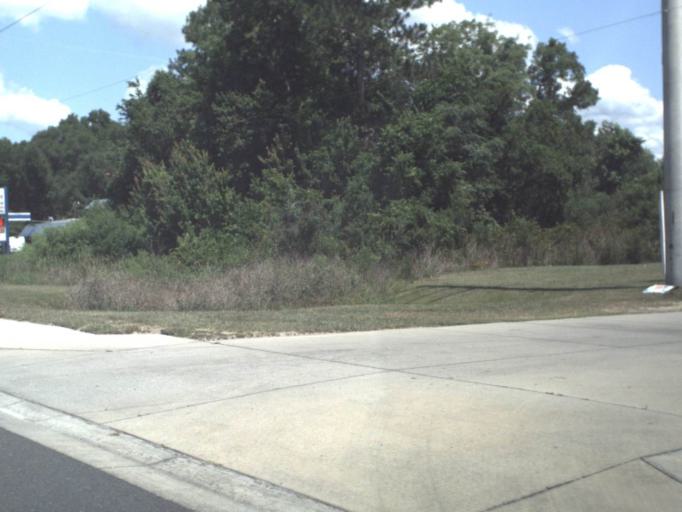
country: US
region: Florida
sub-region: Putnam County
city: Interlachen
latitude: 29.6271
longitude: -81.8631
